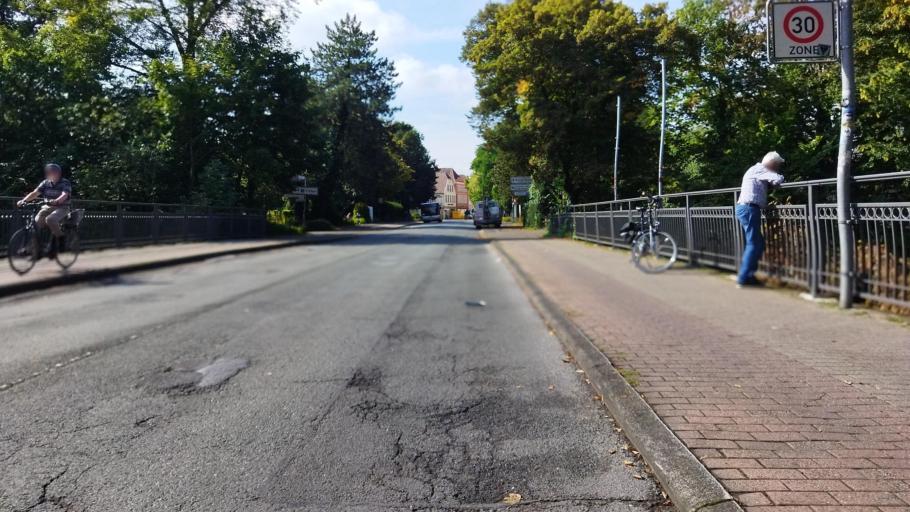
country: DE
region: North Rhine-Westphalia
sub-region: Regierungsbezirk Munster
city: Warendorf
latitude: 51.9551
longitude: 7.9927
